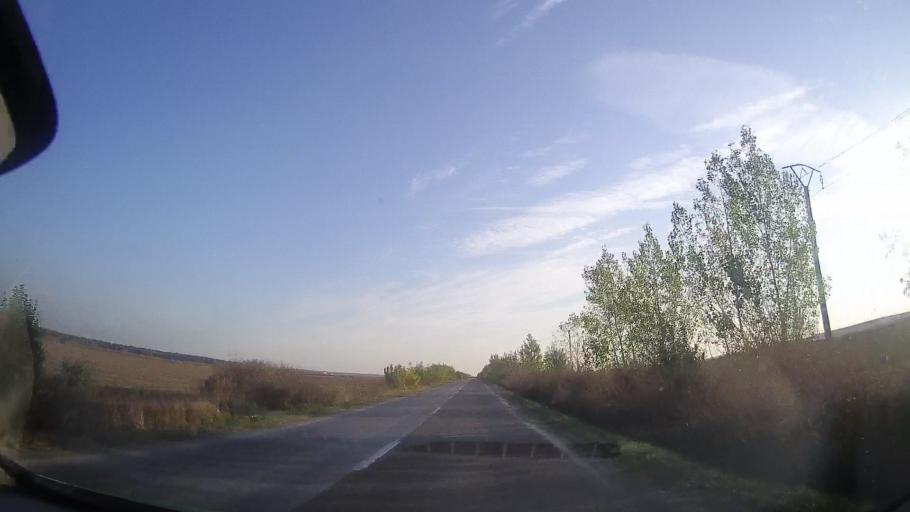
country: RO
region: Timis
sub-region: Comuna Pischia
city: Pischia
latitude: 45.8728
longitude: 21.3259
